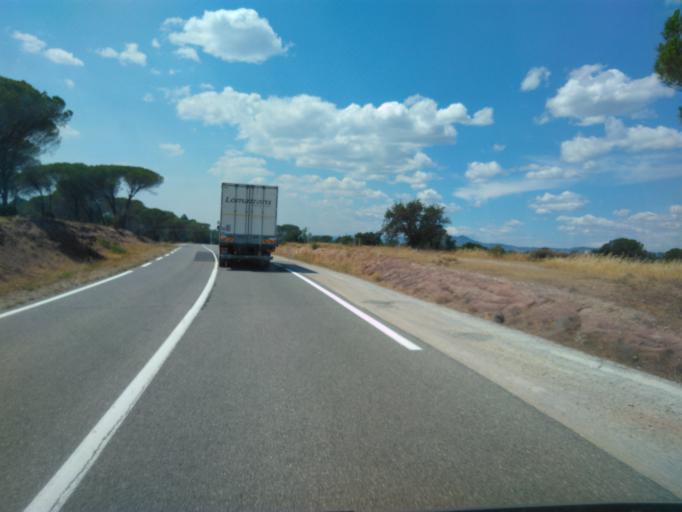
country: FR
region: Provence-Alpes-Cote d'Azur
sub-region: Departement du Var
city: La Garde-Freinet
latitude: 43.3508
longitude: 6.4248
